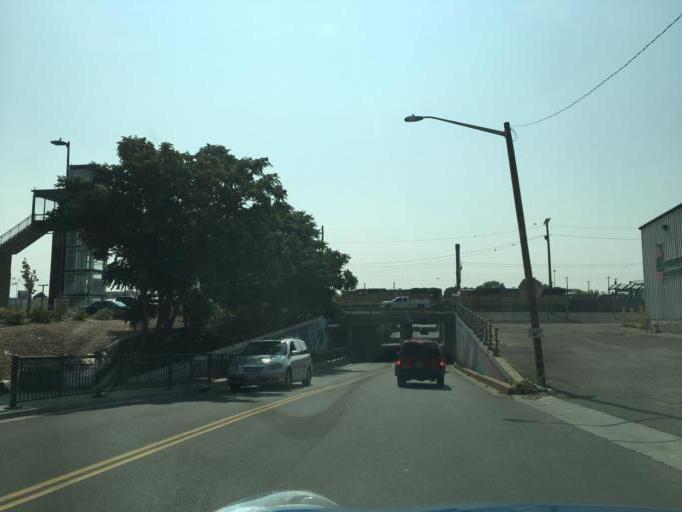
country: US
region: Colorado
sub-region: Denver County
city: Denver
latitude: 39.7720
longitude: -104.9742
